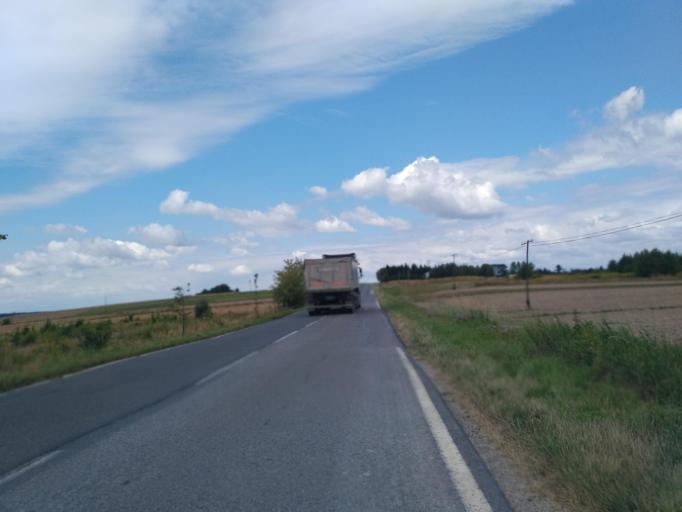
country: PL
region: Subcarpathian Voivodeship
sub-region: Powiat przeworski
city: Jawornik Polski
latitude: 49.8900
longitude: 22.2387
